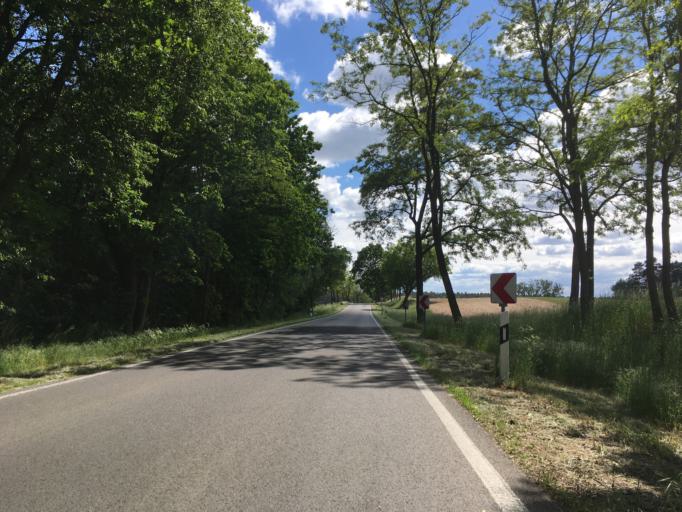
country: DE
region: Brandenburg
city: Protzel
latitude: 52.6706
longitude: 13.9915
